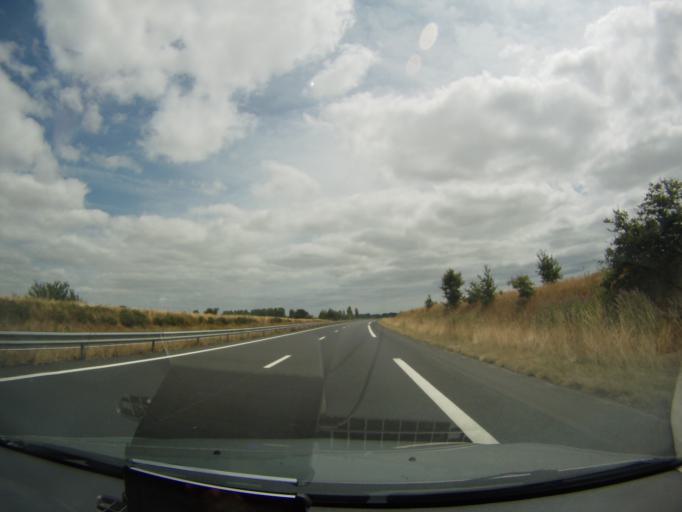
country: FR
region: Pays de la Loire
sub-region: Departement de Maine-et-Loire
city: Roussay
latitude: 47.1073
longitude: -1.0331
